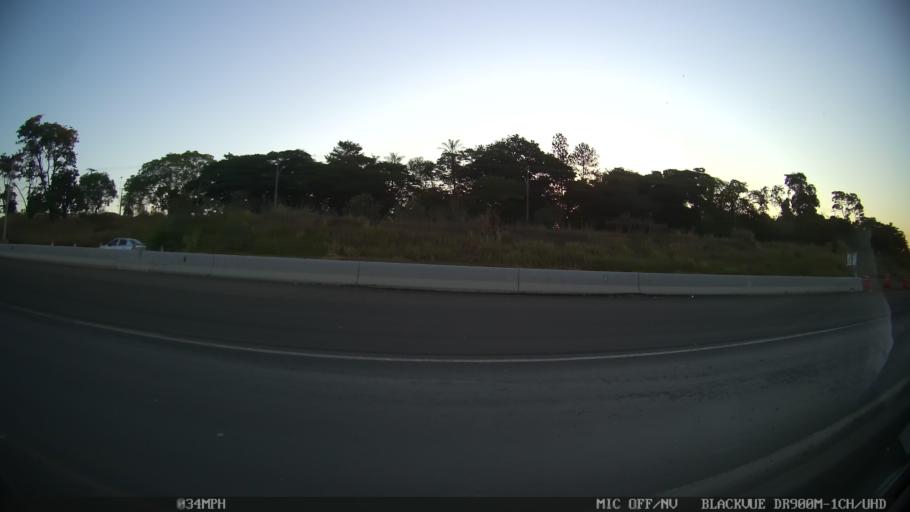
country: BR
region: Sao Paulo
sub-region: Sao Jose Do Rio Preto
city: Sao Jose do Rio Preto
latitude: -20.7802
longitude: -49.3529
